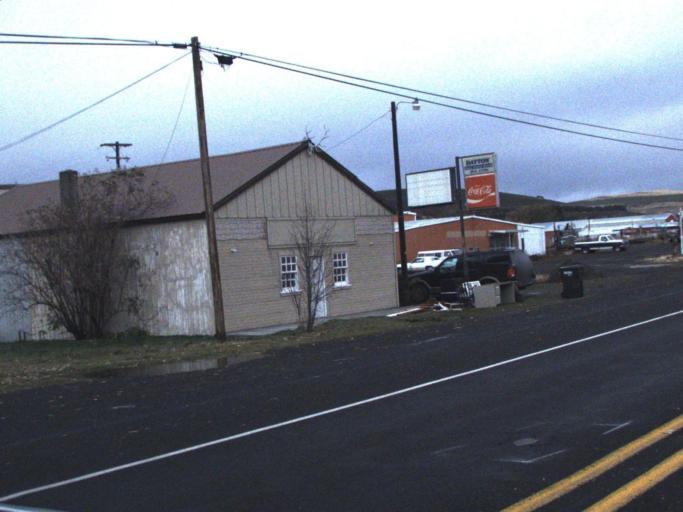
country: US
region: Washington
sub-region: Columbia County
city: Dayton
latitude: 46.3109
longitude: -117.9941
